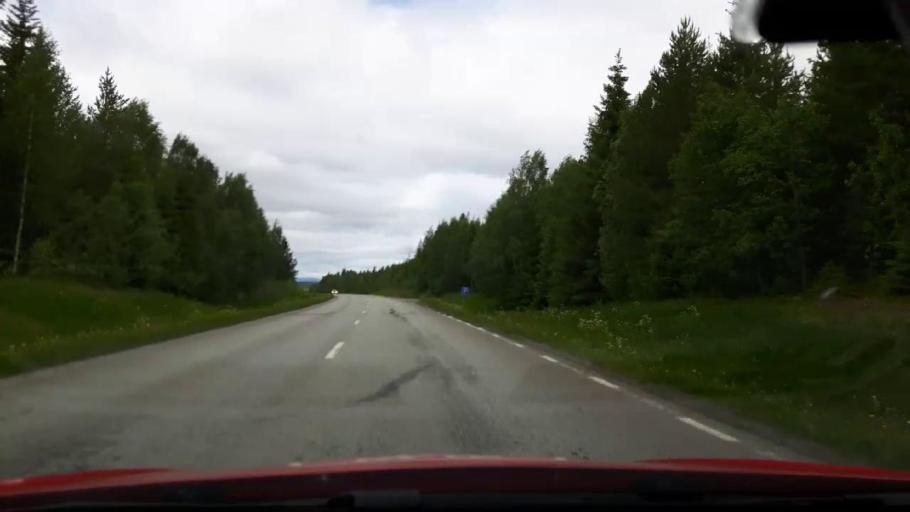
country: SE
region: Jaemtland
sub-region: Krokoms Kommun
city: Krokom
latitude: 63.3897
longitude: 14.5055
